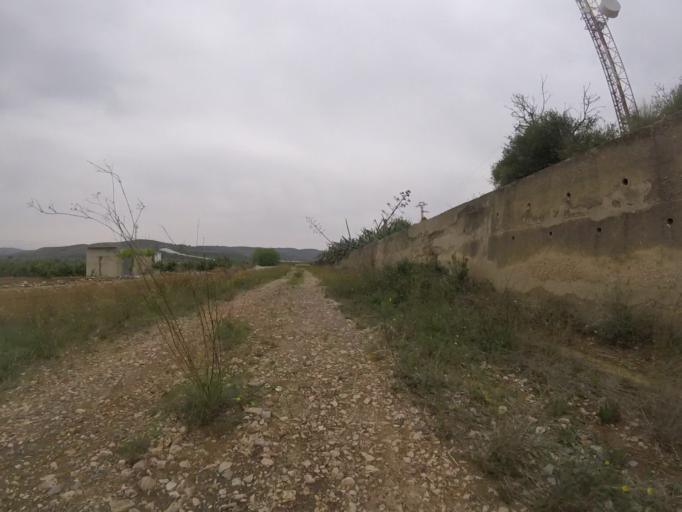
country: ES
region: Valencia
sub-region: Provincia de Castello
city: Alcoceber
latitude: 40.2647
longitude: 0.2578
